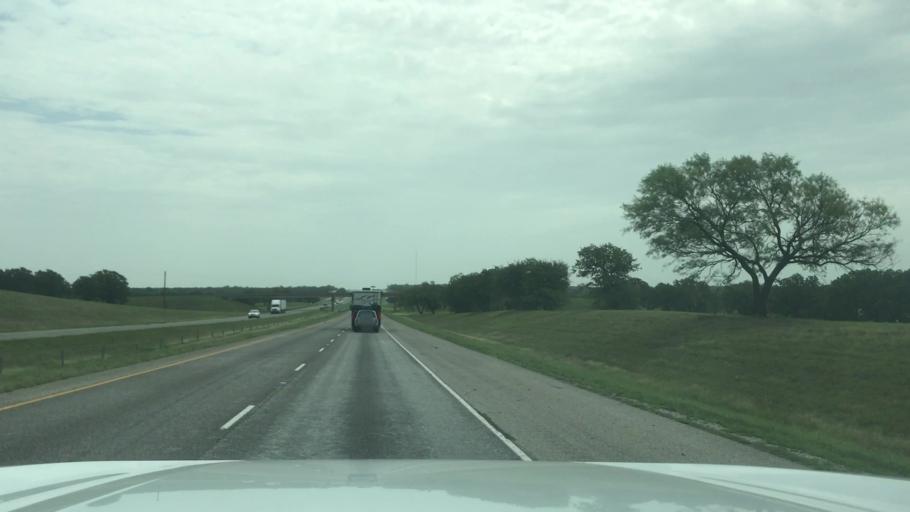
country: US
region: Texas
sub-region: Eastland County
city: Eastland
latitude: 32.3754
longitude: -98.8903
